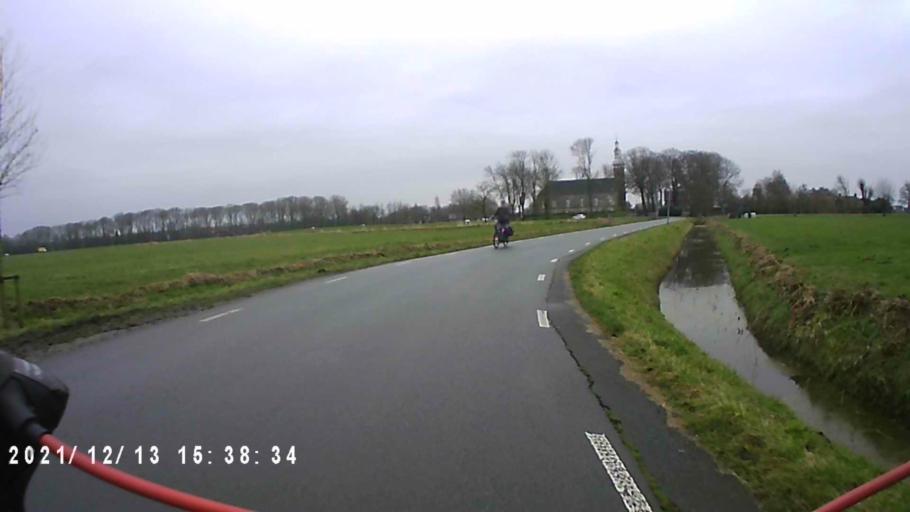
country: NL
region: Groningen
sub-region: Gemeente Appingedam
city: Appingedam
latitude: 53.3251
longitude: 6.8336
